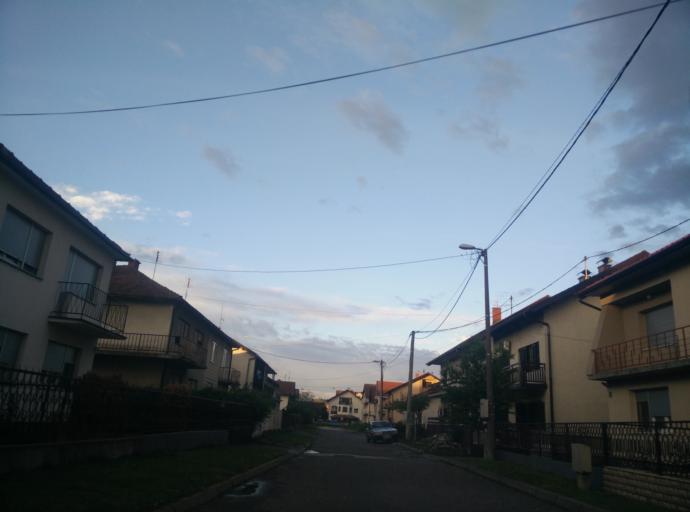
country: BA
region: Brcko
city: Brcko
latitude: 44.8681
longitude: 18.8152
